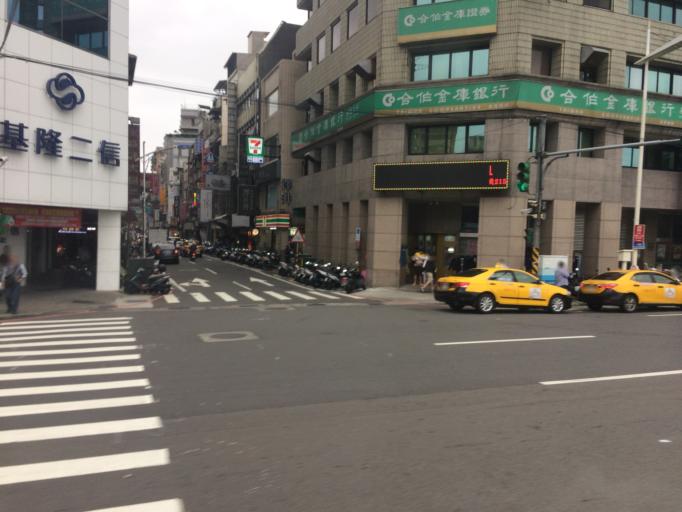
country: TW
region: Taiwan
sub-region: Keelung
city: Keelung
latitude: 25.1298
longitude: 121.7428
